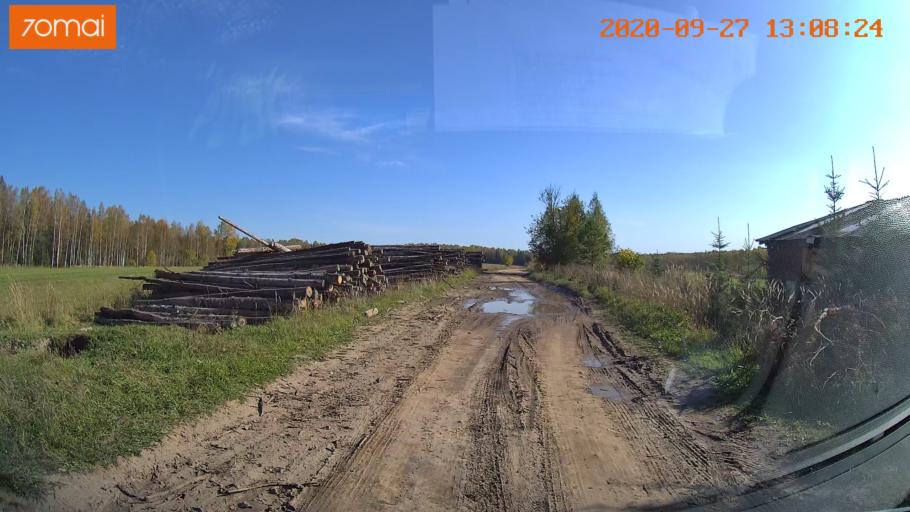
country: RU
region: Ivanovo
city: Furmanov
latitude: 57.1623
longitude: 41.0794
